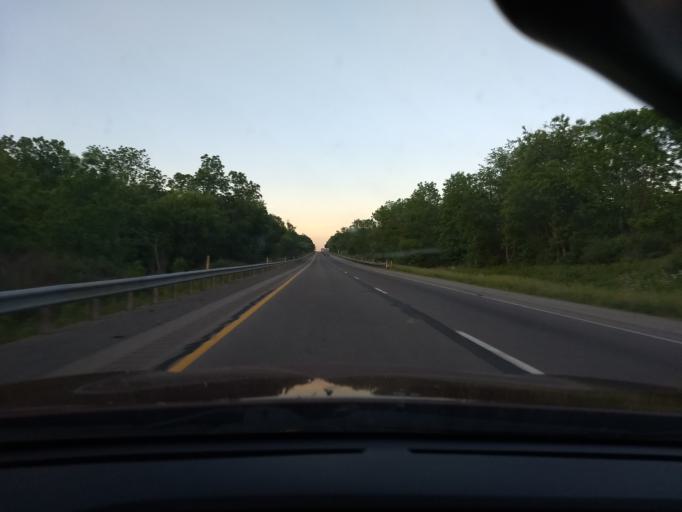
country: US
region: Pennsylvania
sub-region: Centre County
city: Zion
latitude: 40.9571
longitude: -77.6821
